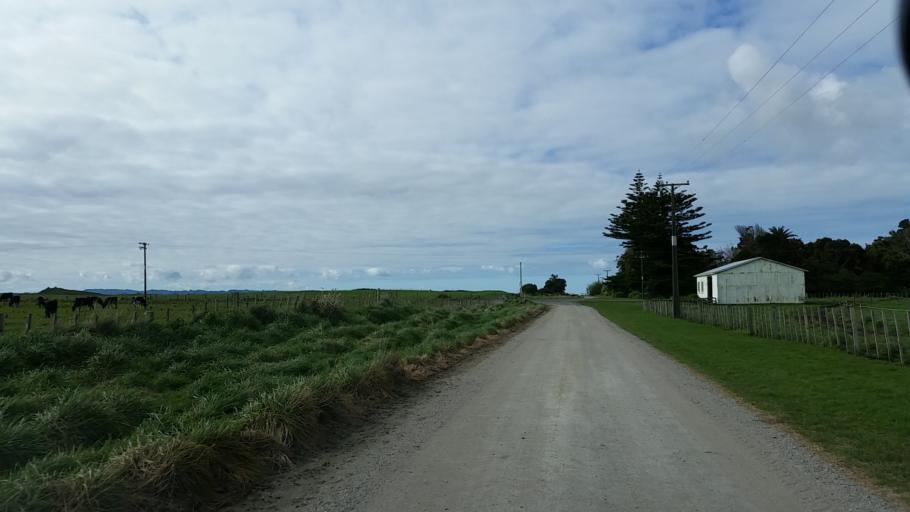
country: NZ
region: Taranaki
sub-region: South Taranaki District
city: Patea
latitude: -39.8074
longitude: 174.6626
